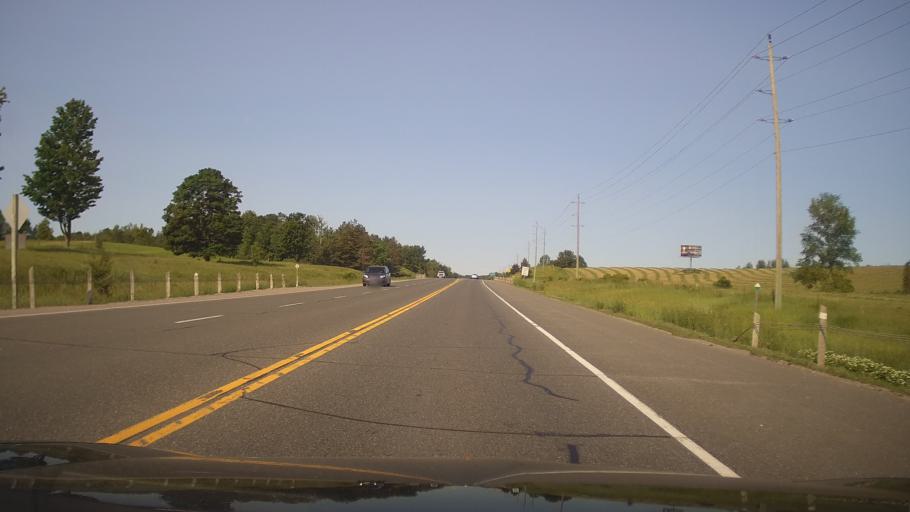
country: CA
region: Ontario
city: Peterborough
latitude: 44.3189
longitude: -78.1778
